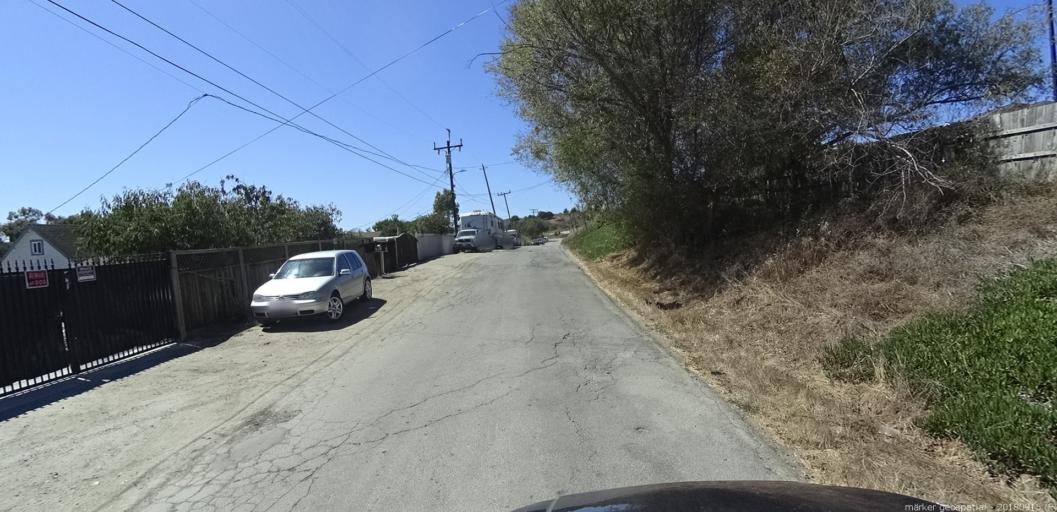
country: US
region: California
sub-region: Monterey County
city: Las Lomas
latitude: 36.8675
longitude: -121.7490
